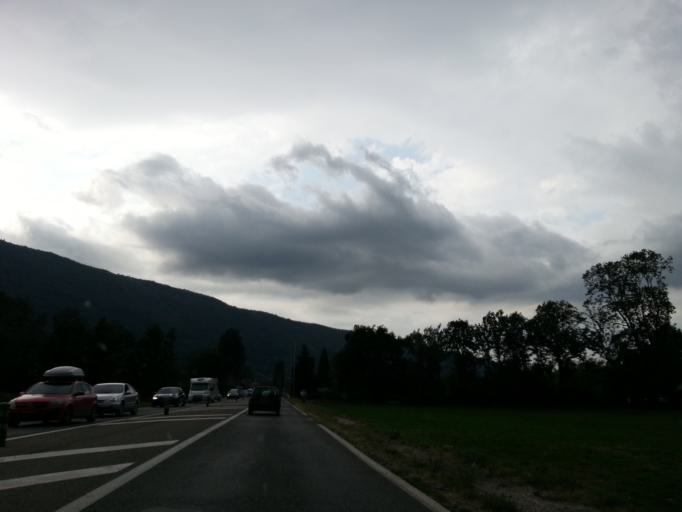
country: FR
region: Rhone-Alpes
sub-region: Departement de la Haute-Savoie
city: Saint-Jorioz
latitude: 45.8406
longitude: 6.1548
